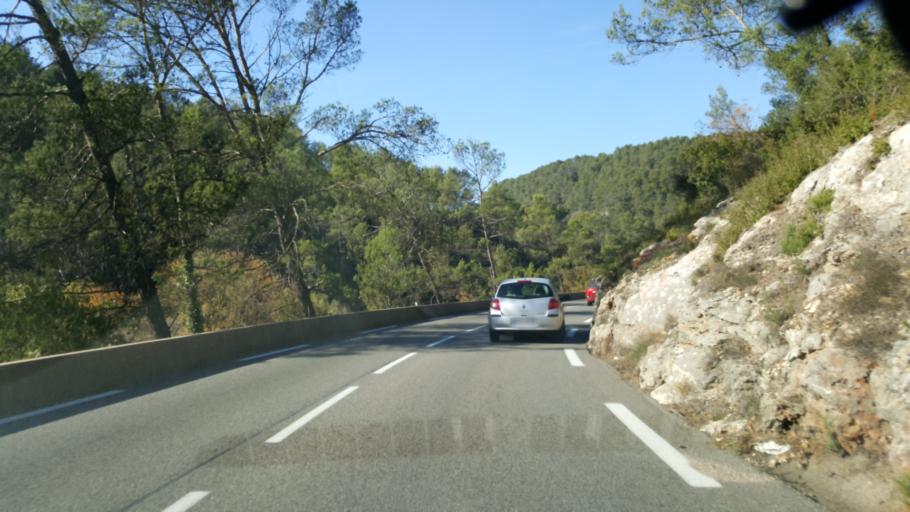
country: FR
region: Provence-Alpes-Cote d'Azur
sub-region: Departement du Var
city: Saint-Zacharie
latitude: 43.3825
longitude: 5.7372
